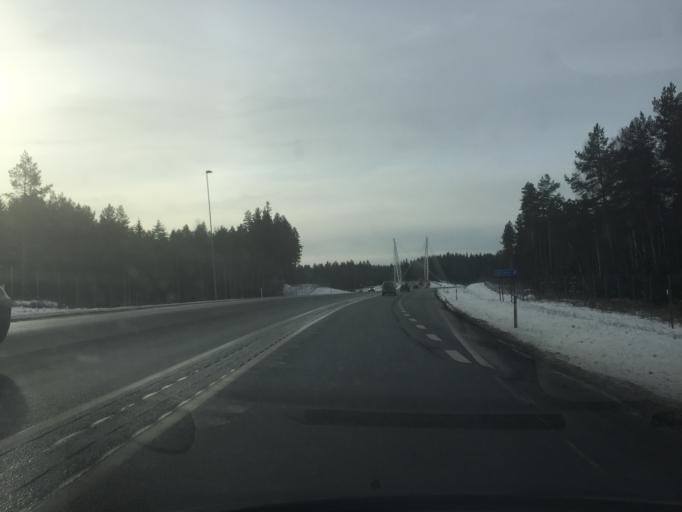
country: NO
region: Hedmark
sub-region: Stange
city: Stange
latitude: 60.7053
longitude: 11.2766
